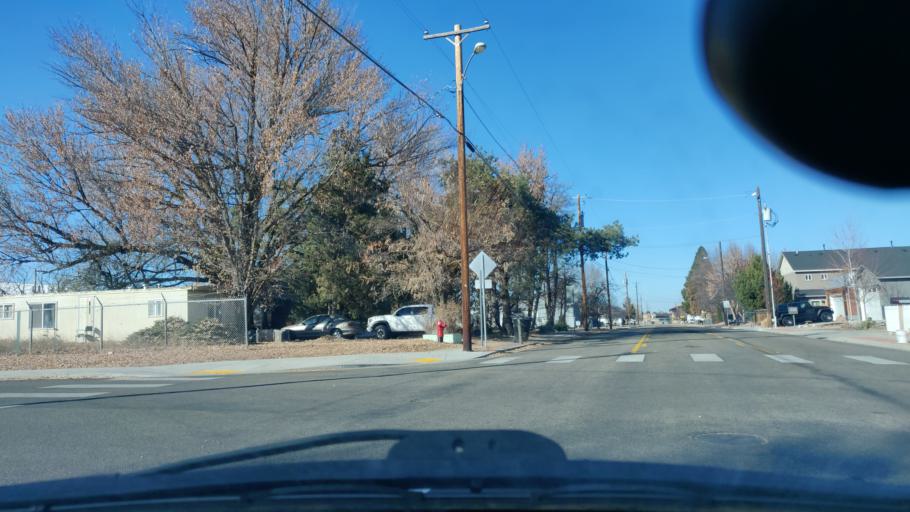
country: US
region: Idaho
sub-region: Ada County
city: Garden City
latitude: 43.6455
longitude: -116.2634
